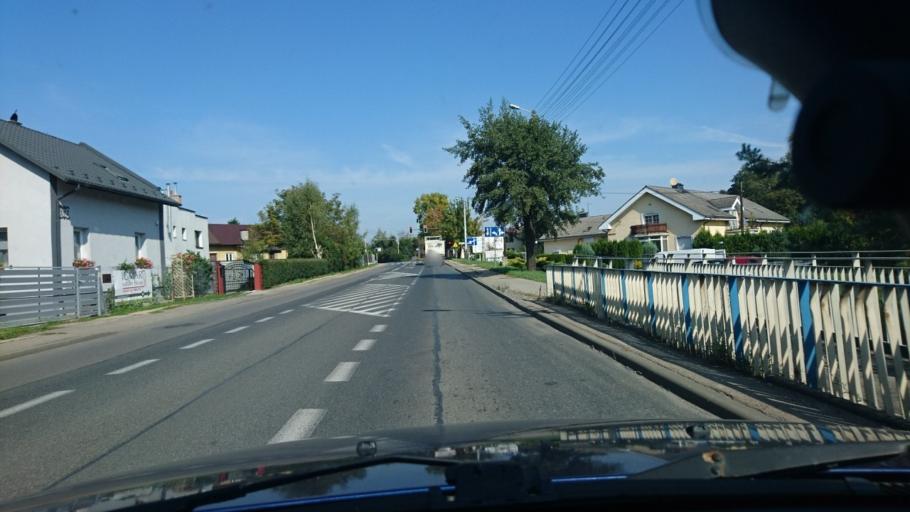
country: PL
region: Silesian Voivodeship
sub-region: Powiat bielski
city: Bestwina
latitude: 49.8826
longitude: 19.0261
